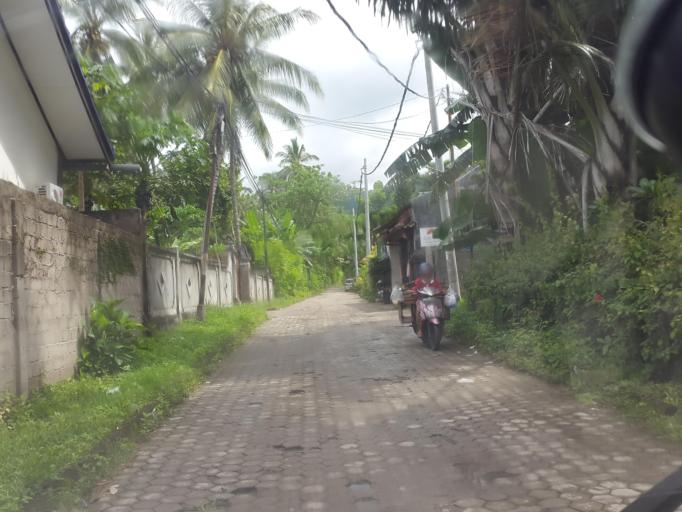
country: ID
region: West Nusa Tenggara
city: Mambalan
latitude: -8.5094
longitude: 116.0595
